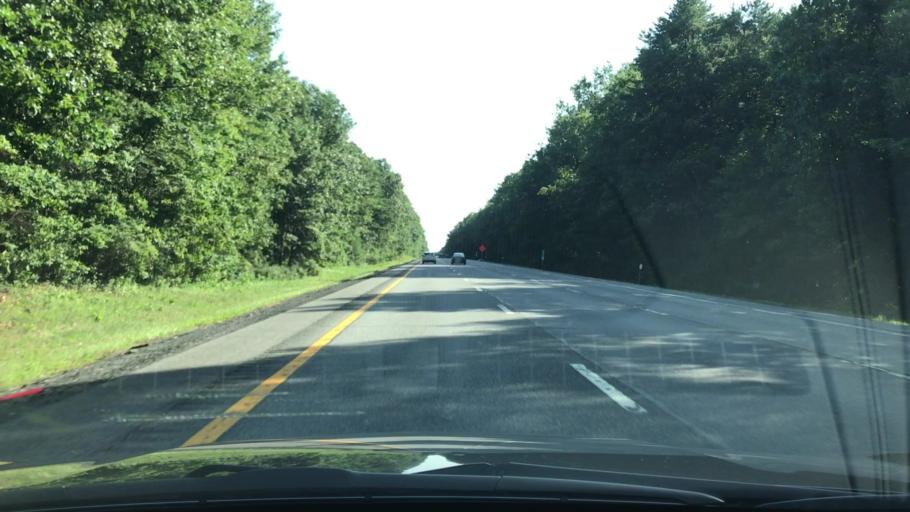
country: US
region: New York
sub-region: Saratoga County
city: Saratoga Springs
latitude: 43.1328
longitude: -73.7345
